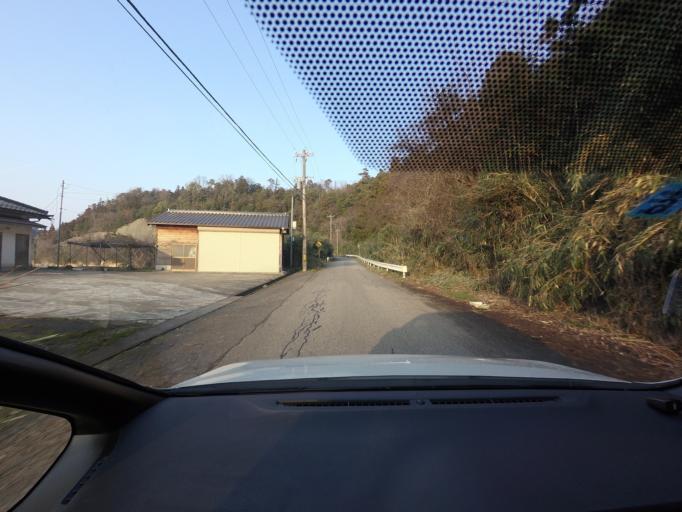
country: JP
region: Ishikawa
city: Nanao
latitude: 37.1440
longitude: 137.0238
